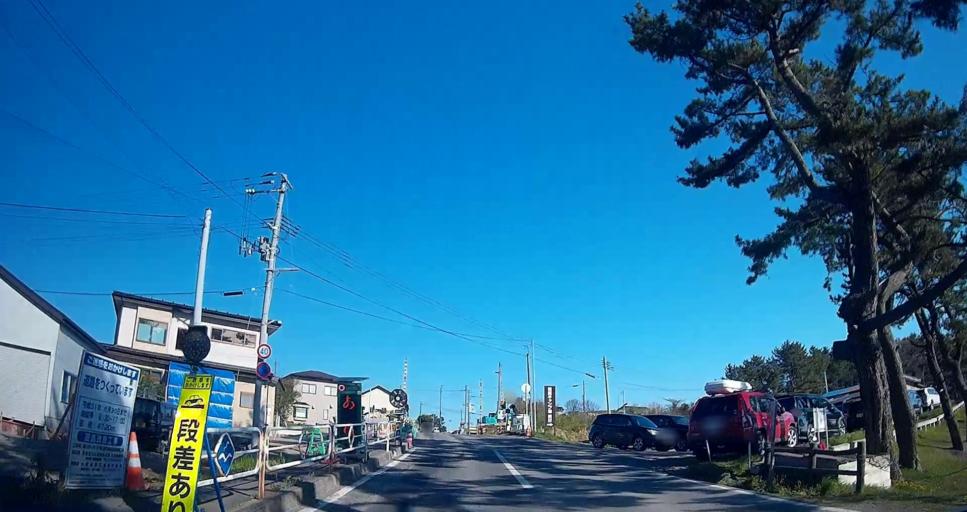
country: JP
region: Aomori
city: Hachinohe
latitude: 40.5099
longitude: 141.6080
